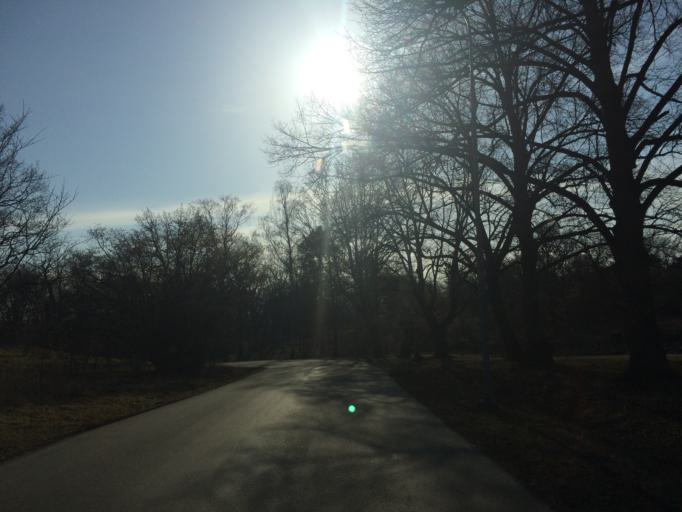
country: SE
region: Stockholm
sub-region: Stockholms Kommun
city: OEstermalm
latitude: 59.3256
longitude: 18.1166
